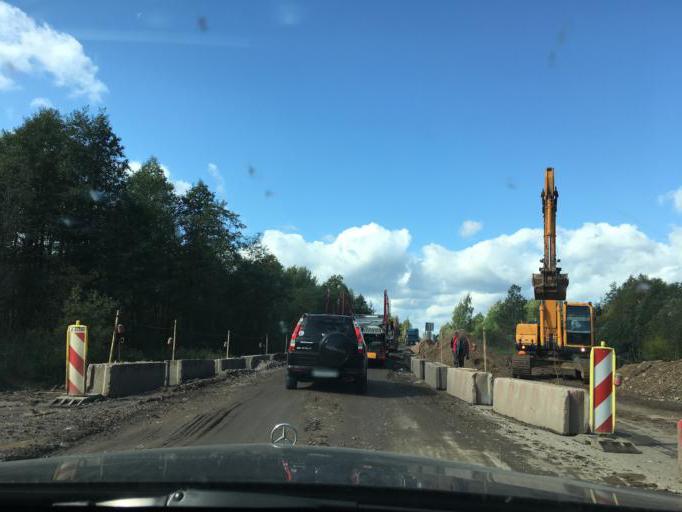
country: RU
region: Pskov
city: Novosokol'niki
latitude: 56.2730
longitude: 30.3445
